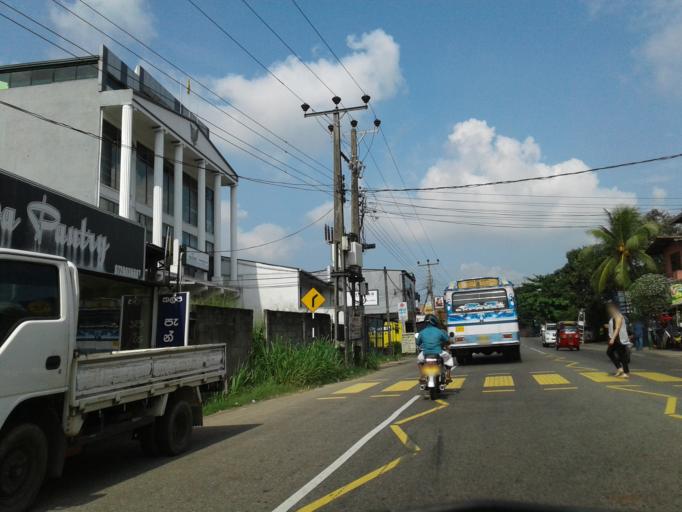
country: LK
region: Western
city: Battaramulla South
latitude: 6.9061
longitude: 79.9478
